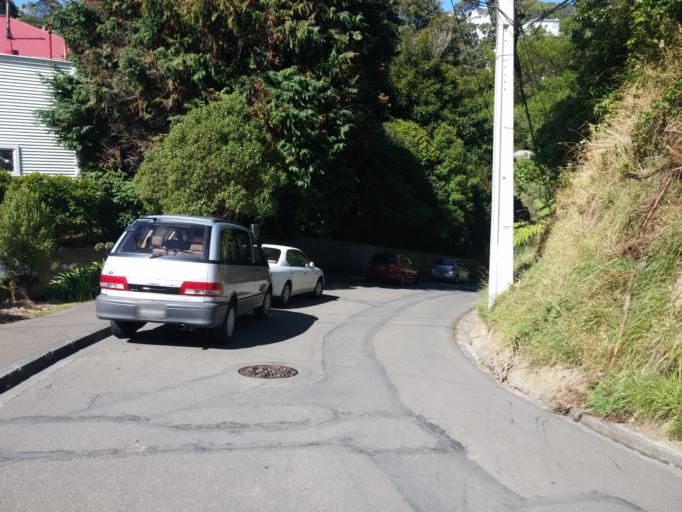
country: NZ
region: Wellington
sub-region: Wellington City
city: Kelburn
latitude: -41.2843
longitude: 174.7597
